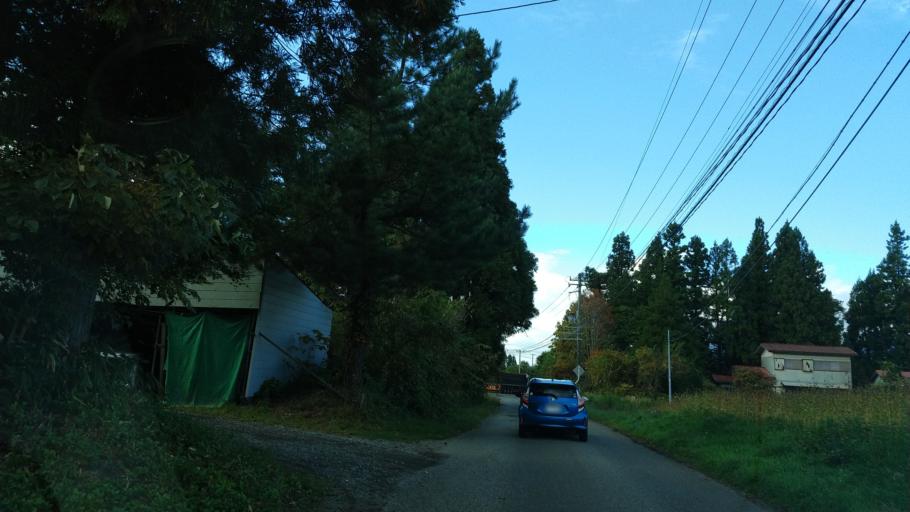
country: JP
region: Fukushima
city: Inawashiro
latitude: 37.5209
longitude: 140.0128
